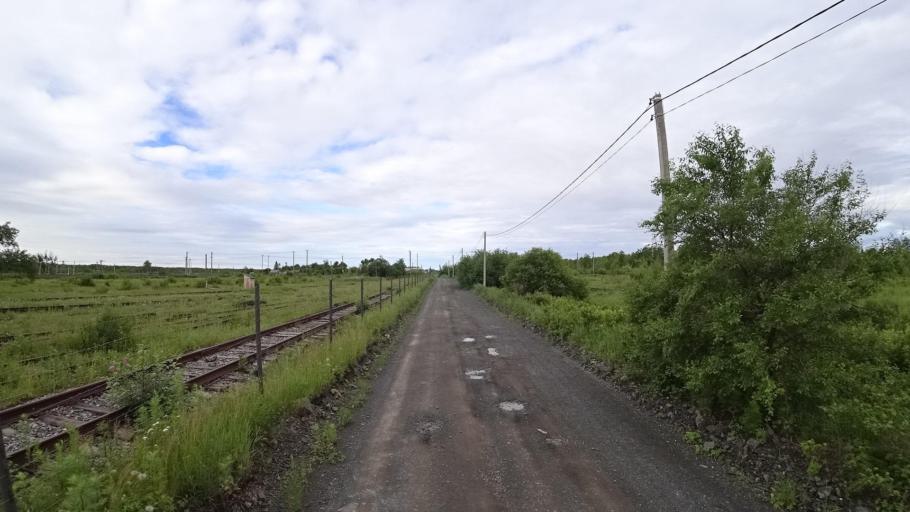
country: RU
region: Khabarovsk Krai
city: Amursk
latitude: 49.9062
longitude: 136.1459
